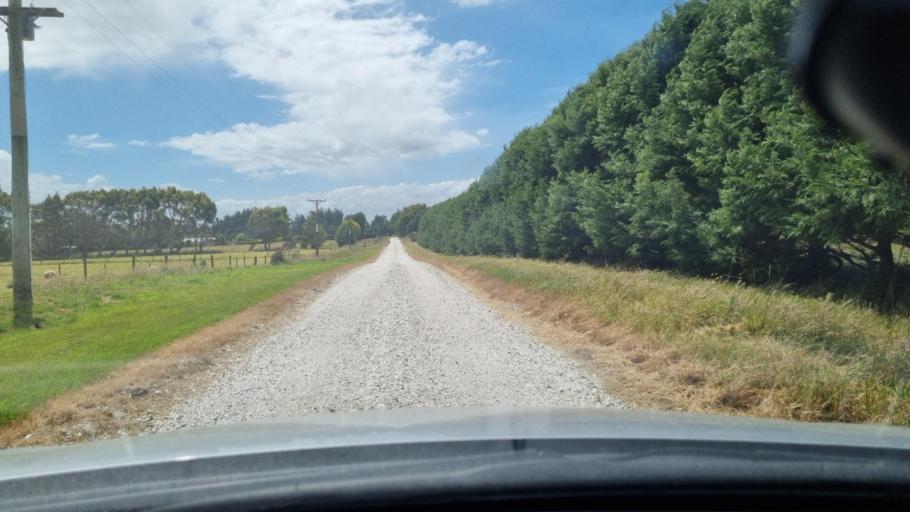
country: NZ
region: Southland
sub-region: Invercargill City
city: Invercargill
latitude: -46.4542
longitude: 168.3884
